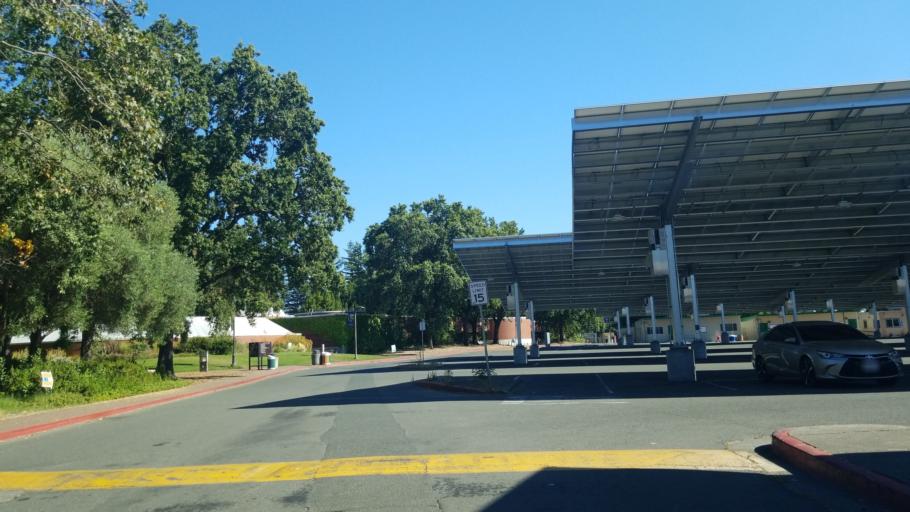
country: US
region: California
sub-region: Sonoma County
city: Santa Rosa
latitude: 38.4564
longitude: -122.7235
